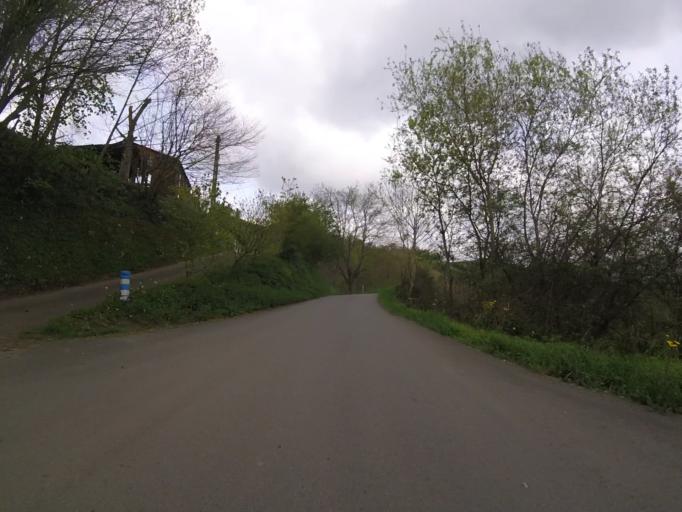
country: ES
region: Basque Country
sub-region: Provincia de Guipuzcoa
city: Anoeta
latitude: 43.1736
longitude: -2.0827
